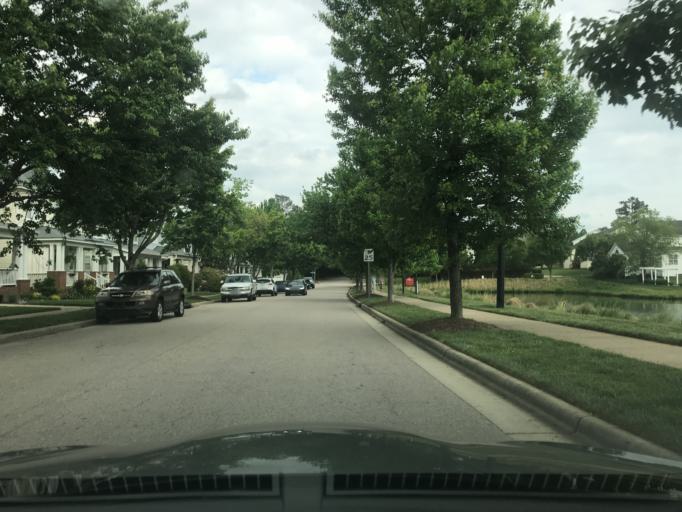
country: US
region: North Carolina
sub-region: Wake County
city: Wake Forest
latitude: 35.9296
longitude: -78.5616
